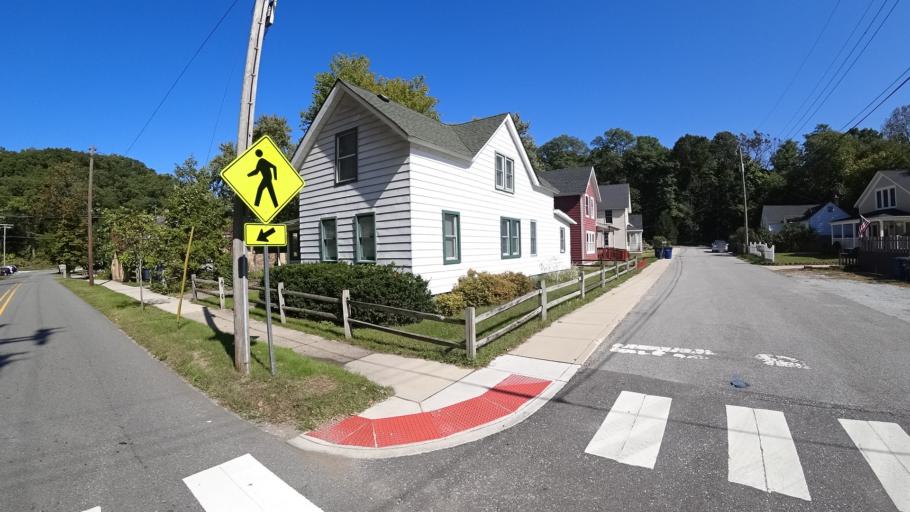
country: US
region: Indiana
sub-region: LaPorte County
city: Michigan City
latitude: 41.7238
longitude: -86.8946
